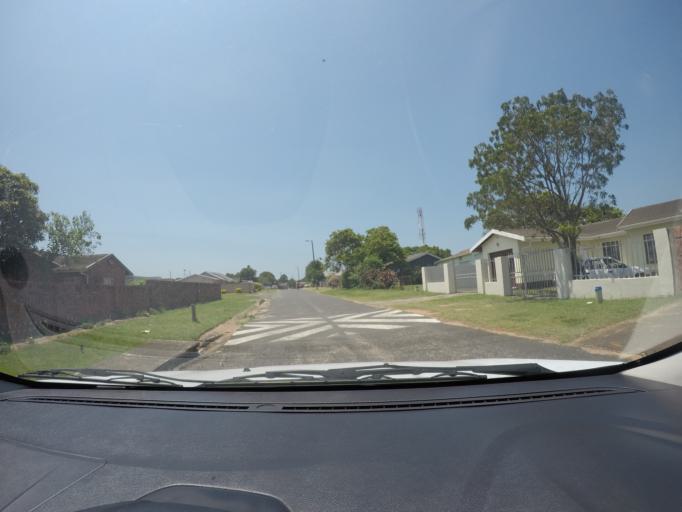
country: ZA
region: KwaZulu-Natal
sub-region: uThungulu District Municipality
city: eSikhawini
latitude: -28.8732
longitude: 31.9150
